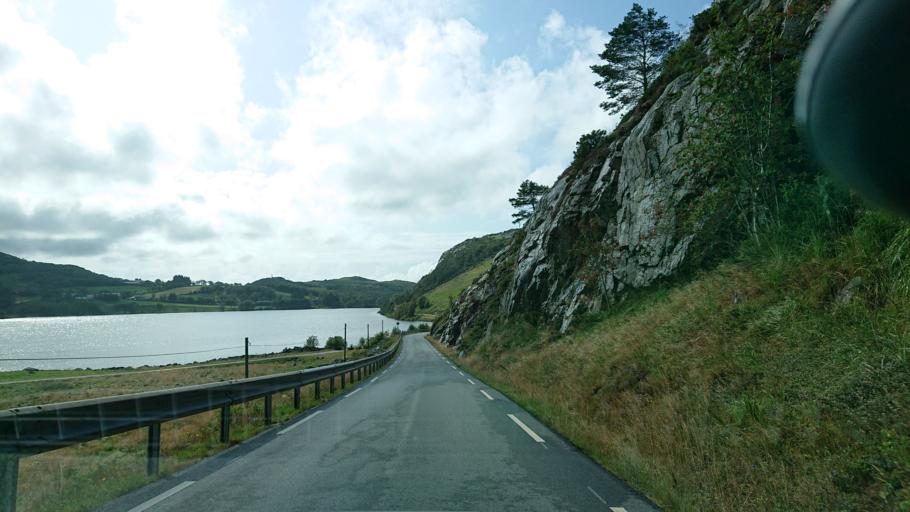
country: NO
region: Rogaland
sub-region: Gjesdal
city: Algard
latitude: 58.6773
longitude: 5.8414
